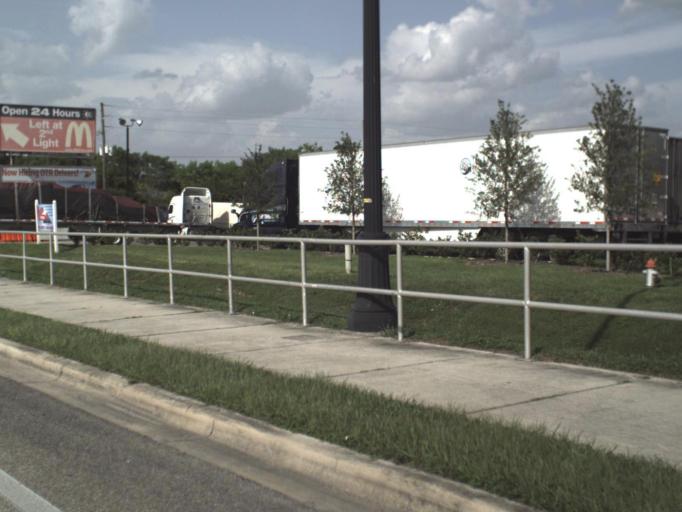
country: US
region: Florida
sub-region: Polk County
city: Haines City
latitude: 28.1188
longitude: -81.6396
